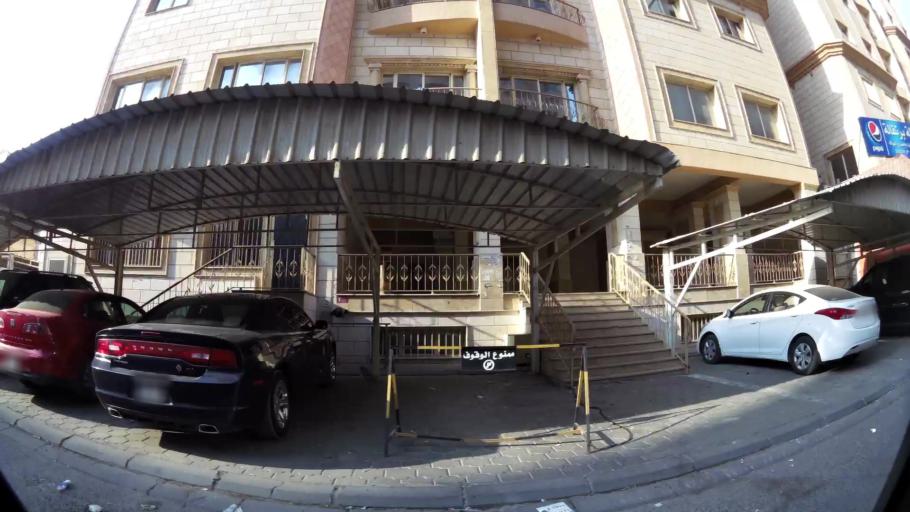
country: KW
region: Muhafazat Hawalli
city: As Salimiyah
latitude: 29.3342
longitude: 48.0575
